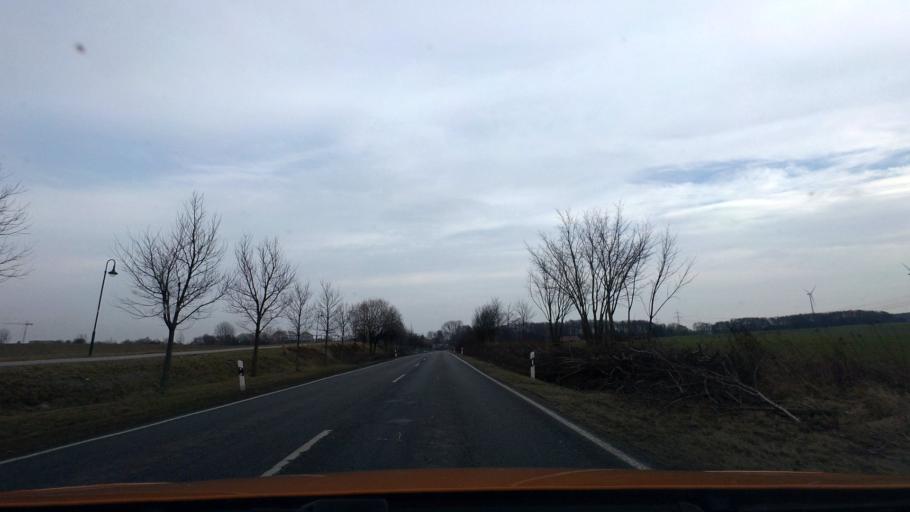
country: DE
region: Berlin
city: Buch
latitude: 52.6271
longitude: 13.5355
